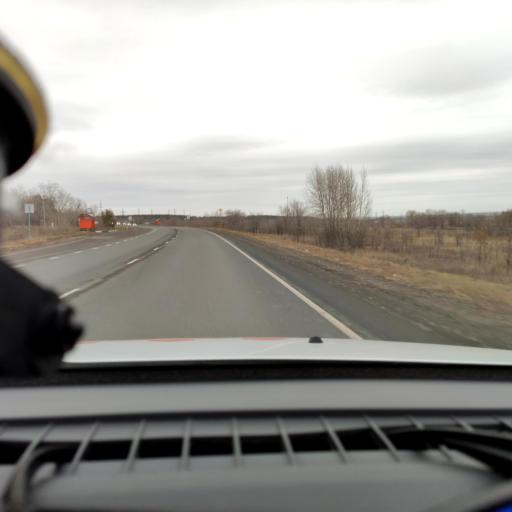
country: RU
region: Samara
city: Samara
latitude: 53.1235
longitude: 50.1914
